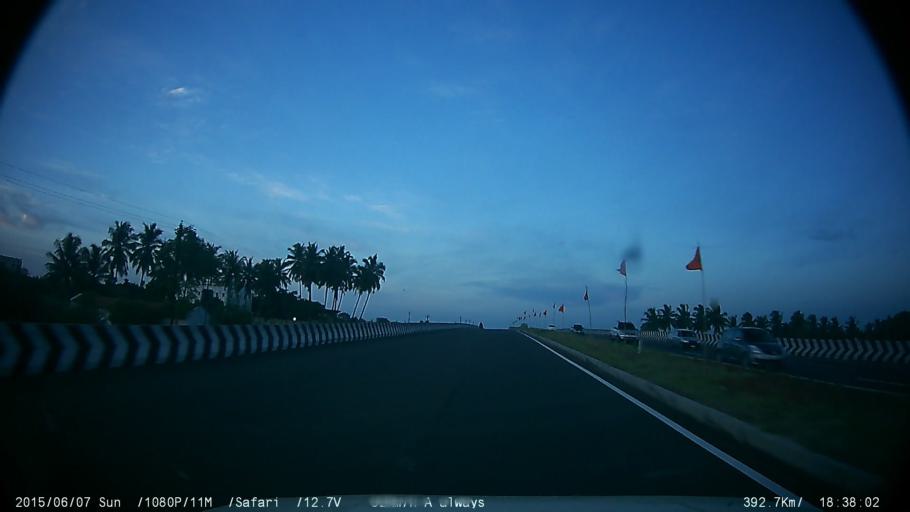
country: IN
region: Tamil Nadu
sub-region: Tiruppur
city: Avinashi
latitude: 11.2019
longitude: 77.3255
